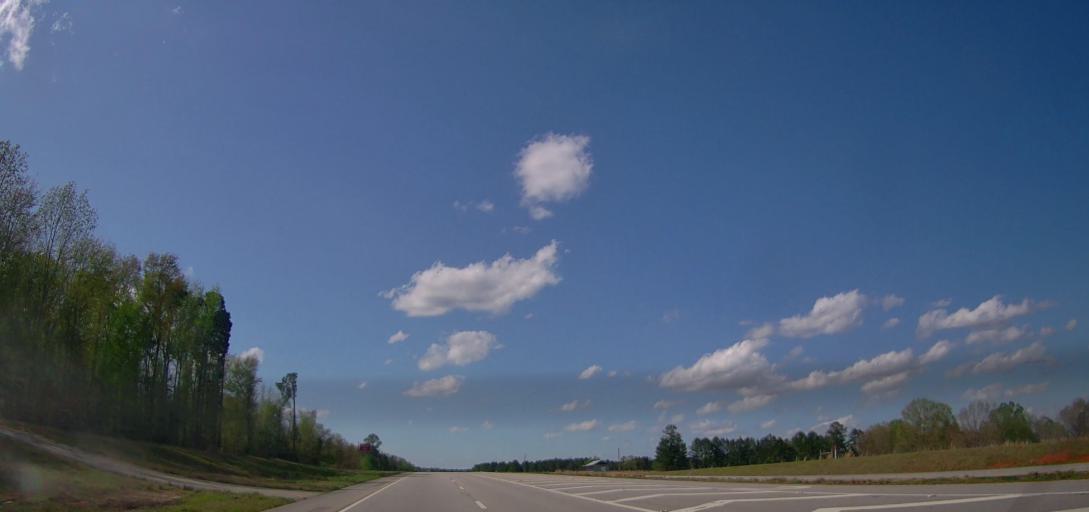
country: US
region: Georgia
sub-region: Baldwin County
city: Hardwick
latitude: 33.0237
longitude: -83.1041
